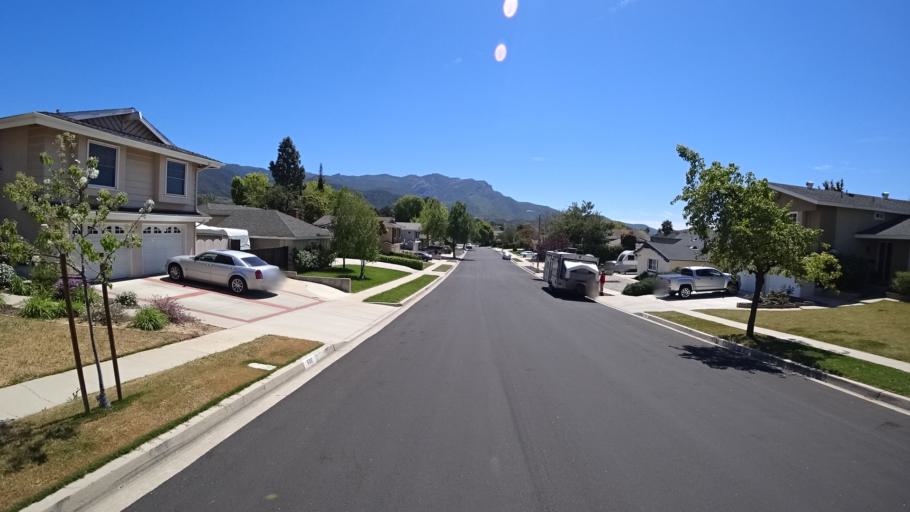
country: US
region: California
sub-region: Ventura County
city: Casa Conejo
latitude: 34.1633
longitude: -118.9528
